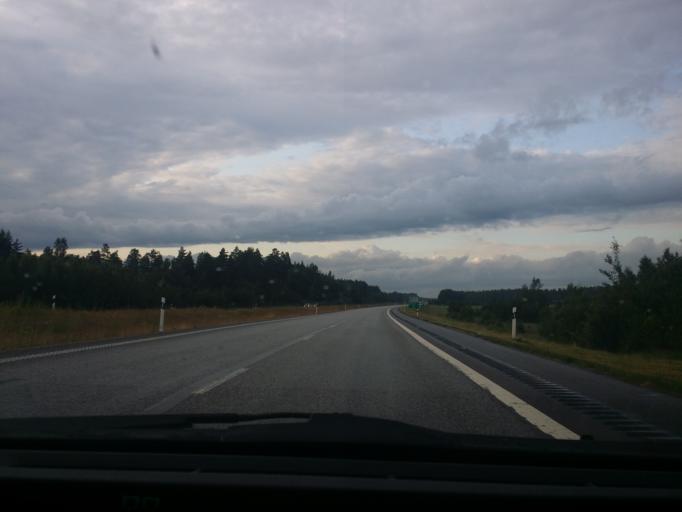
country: SE
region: Vaestmanland
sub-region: Arboga Kommun
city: Arboga
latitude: 59.4666
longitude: 15.9001
